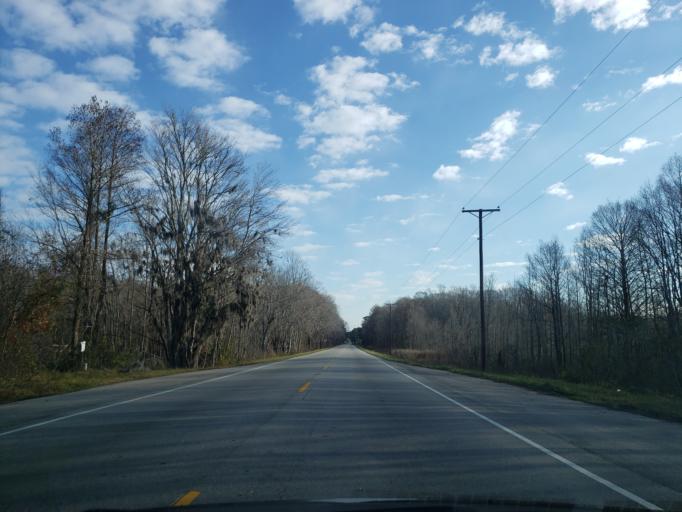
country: US
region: Georgia
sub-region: Chatham County
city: Port Wentworth
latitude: 32.1769
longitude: -81.0869
